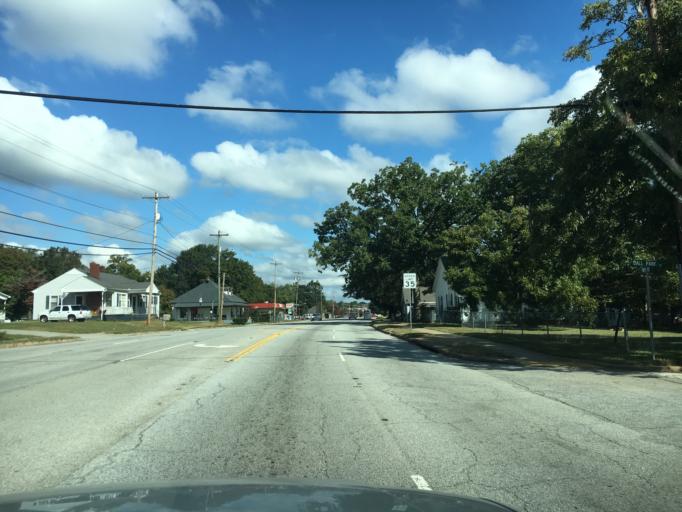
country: US
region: South Carolina
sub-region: Greenville County
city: Greer
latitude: 34.9284
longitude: -82.2225
